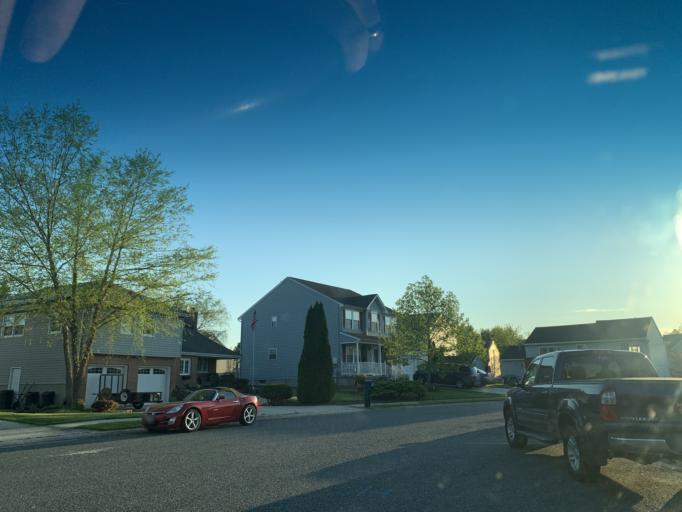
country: US
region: Maryland
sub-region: Harford County
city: Aberdeen
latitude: 39.5127
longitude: -76.1883
